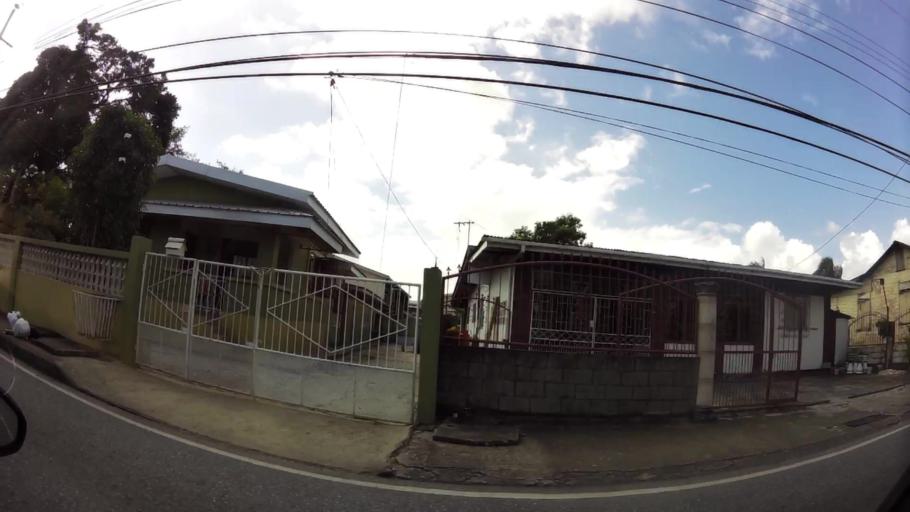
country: TT
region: Borough of Arima
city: Arima
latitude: 10.6340
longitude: -61.2761
